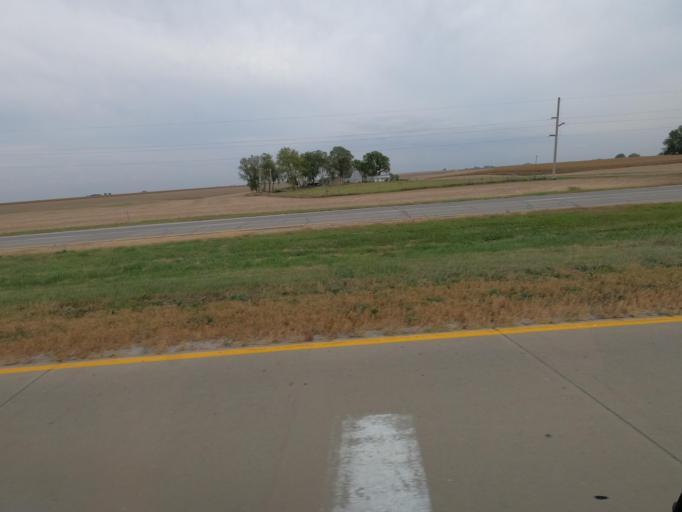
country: US
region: Iowa
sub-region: Jasper County
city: Monroe
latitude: 41.4487
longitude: -93.0234
